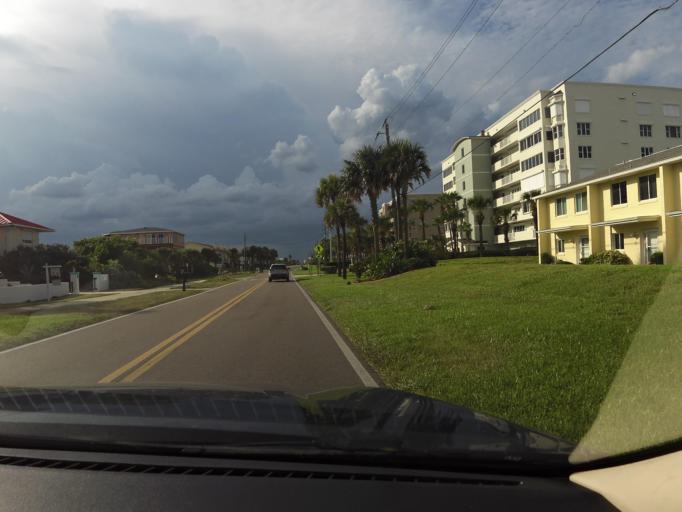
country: US
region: Florida
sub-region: Volusia County
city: Ponce Inlet
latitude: 29.0920
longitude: -80.9319
